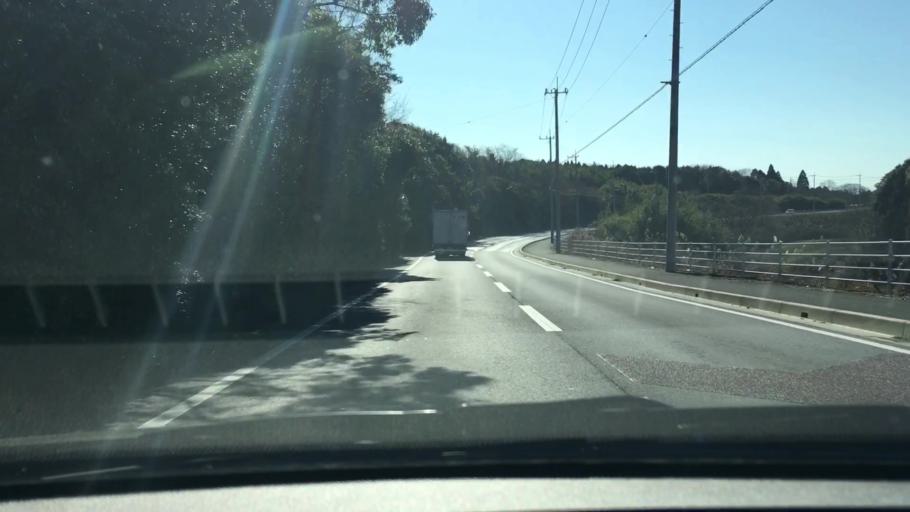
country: JP
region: Chiba
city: Narita
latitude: 35.7337
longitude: 140.4000
